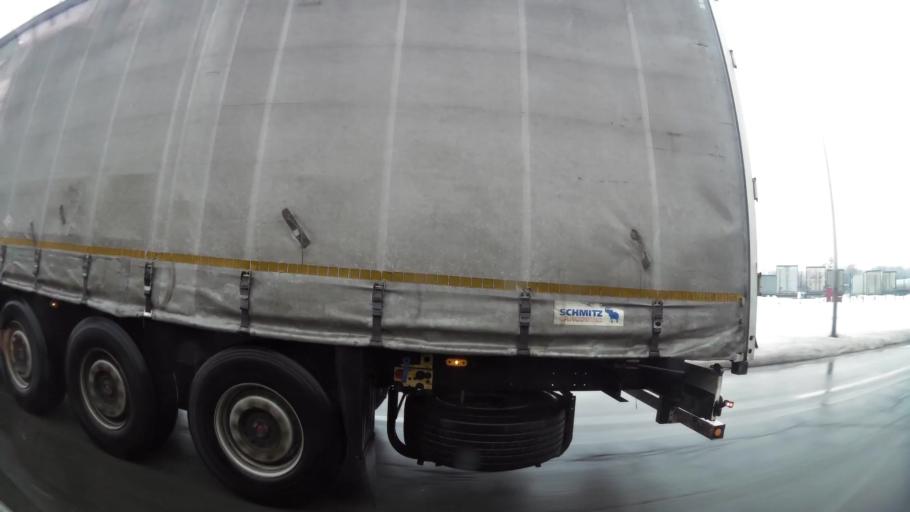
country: RS
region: Central Serbia
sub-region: Belgrade
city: Zemun
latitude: 44.8282
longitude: 20.3626
